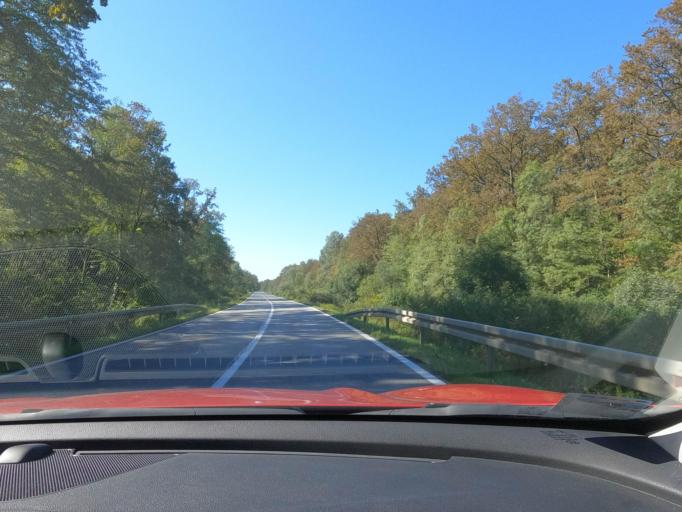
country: HR
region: Sisacko-Moslavacka
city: Budasevo
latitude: 45.5040
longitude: 16.5173
